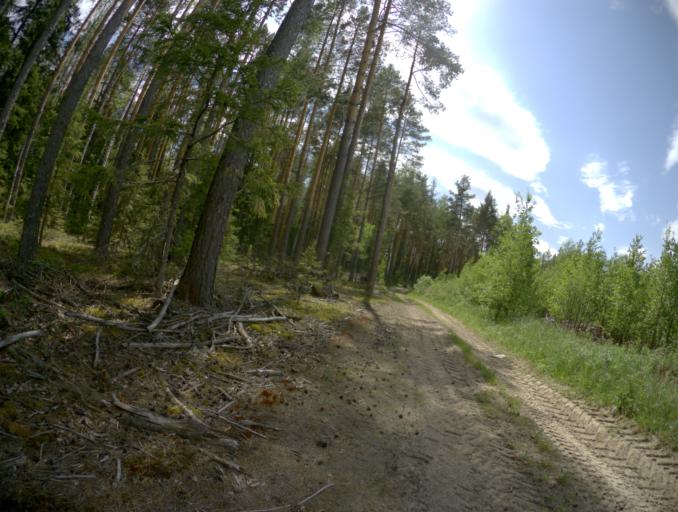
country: RU
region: Vladimir
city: Ivanishchi
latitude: 55.7050
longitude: 40.4546
